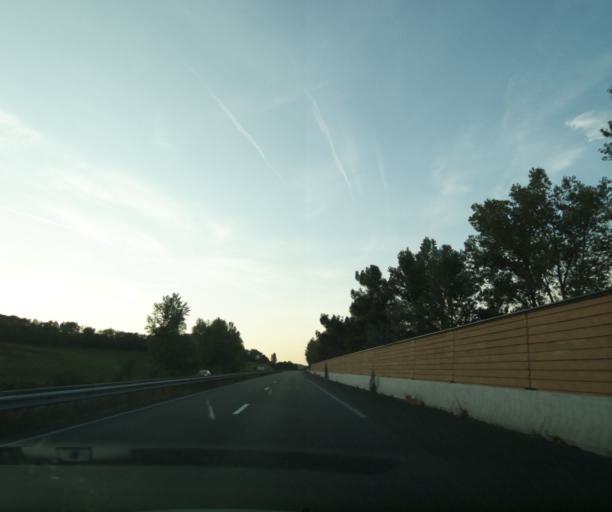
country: FR
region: Aquitaine
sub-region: Departement du Lot-et-Garonne
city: Buzet-sur-Baise
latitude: 44.2579
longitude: 0.2888
